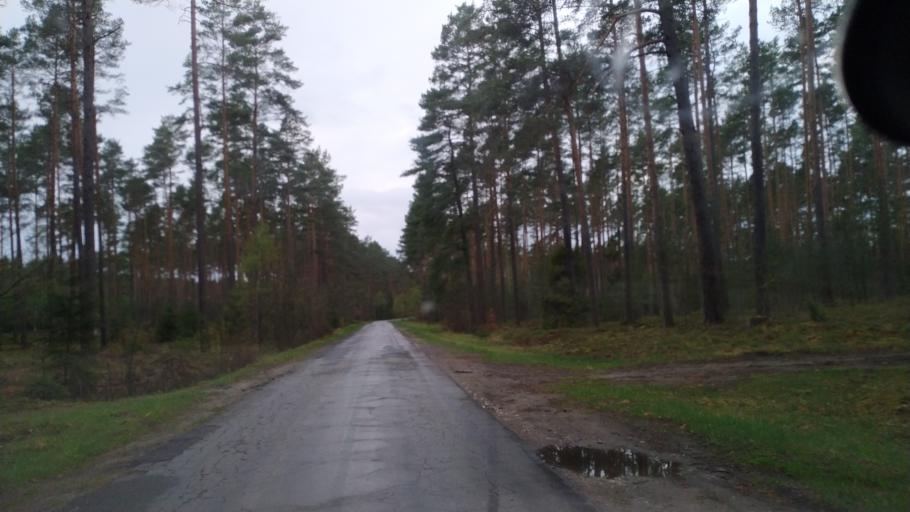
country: PL
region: Pomeranian Voivodeship
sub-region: Powiat starogardzki
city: Osiek
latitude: 53.6796
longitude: 18.4951
